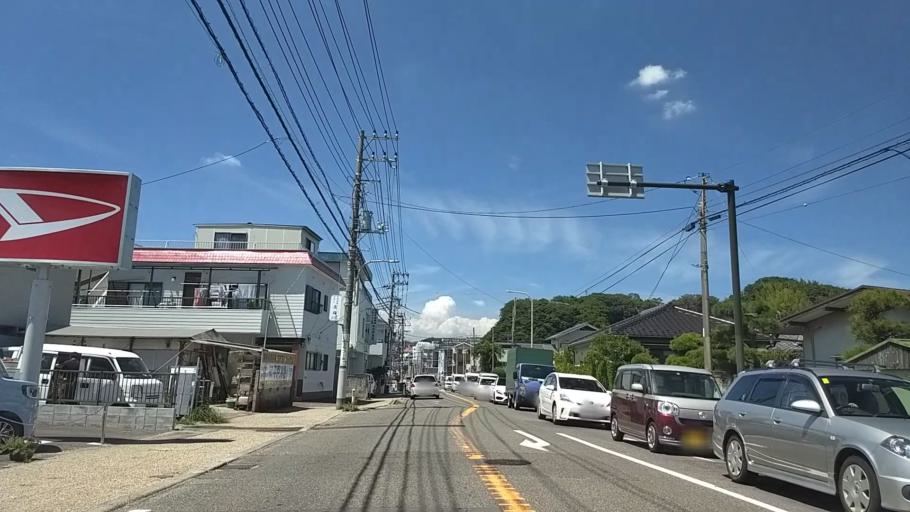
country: JP
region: Kanagawa
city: Zushi
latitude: 35.2976
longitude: 139.5950
